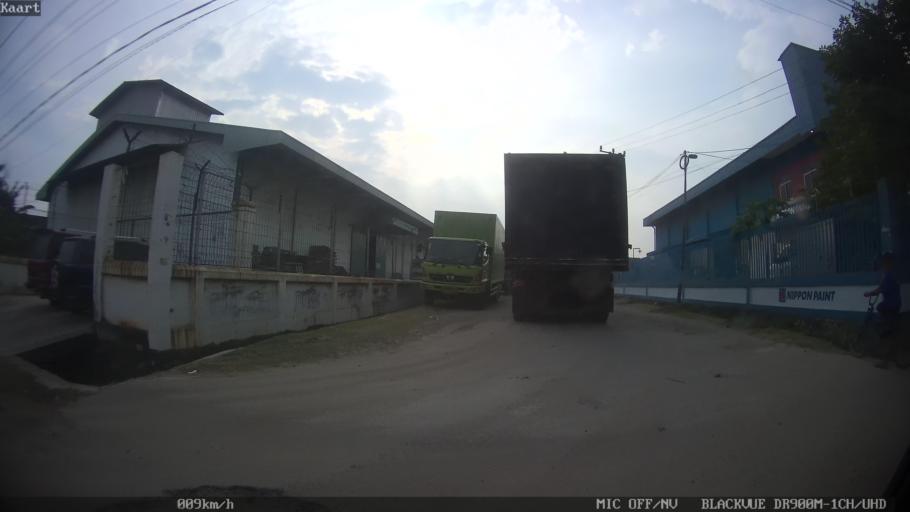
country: ID
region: Lampung
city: Panjang
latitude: -5.4468
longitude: 105.3102
